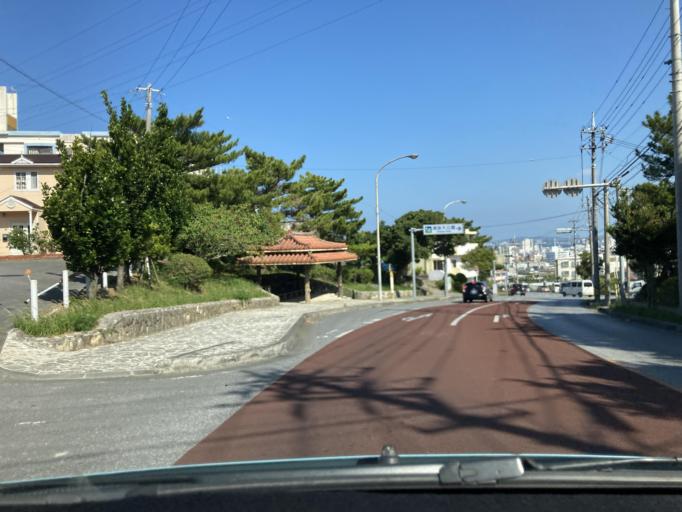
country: JP
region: Okinawa
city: Ginowan
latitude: 26.2558
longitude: 127.7240
